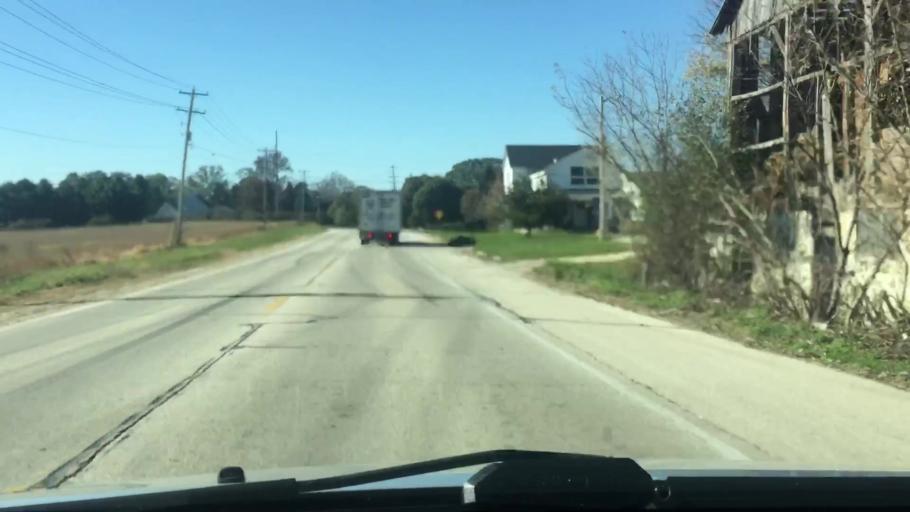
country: US
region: Wisconsin
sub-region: Waukesha County
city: Wales
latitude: 42.9881
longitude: -88.3075
